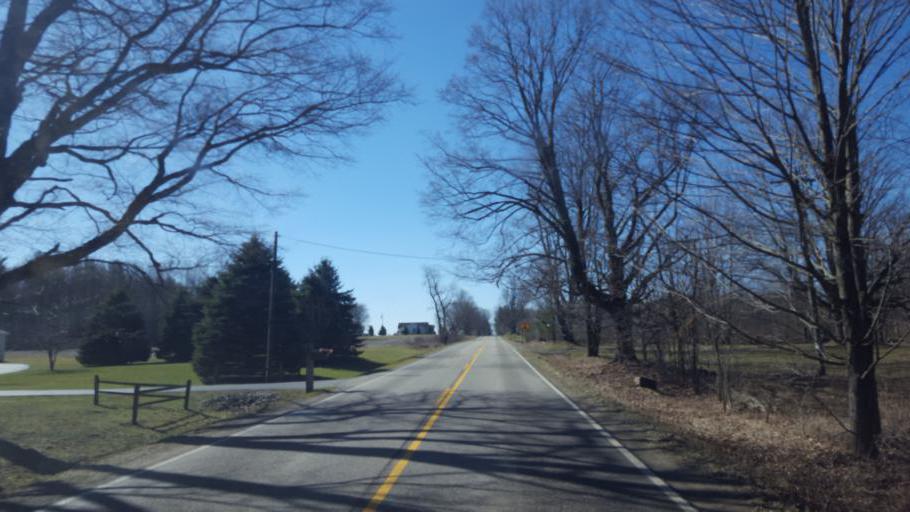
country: US
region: Michigan
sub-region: Montcalm County
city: Edmore
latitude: 43.5271
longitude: -85.0260
